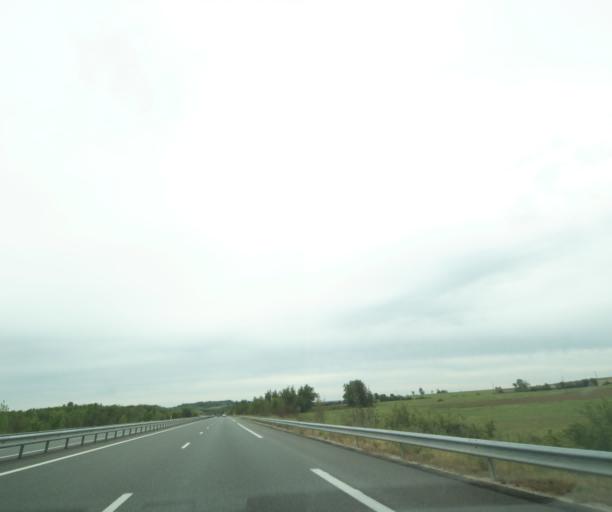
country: FR
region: Midi-Pyrenees
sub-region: Departement du Lot
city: Lalbenque
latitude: 44.2858
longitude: 1.5058
